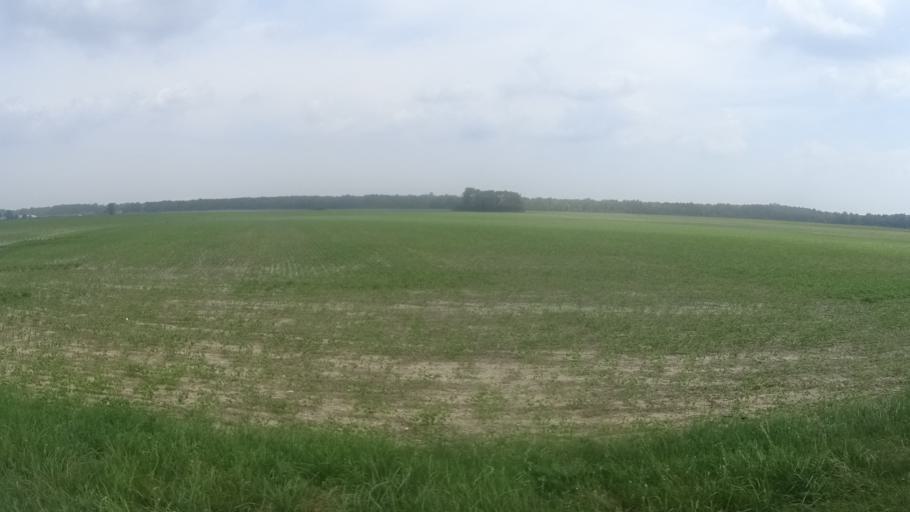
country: US
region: Ohio
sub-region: Erie County
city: Milan
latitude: 41.3469
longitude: -82.6879
